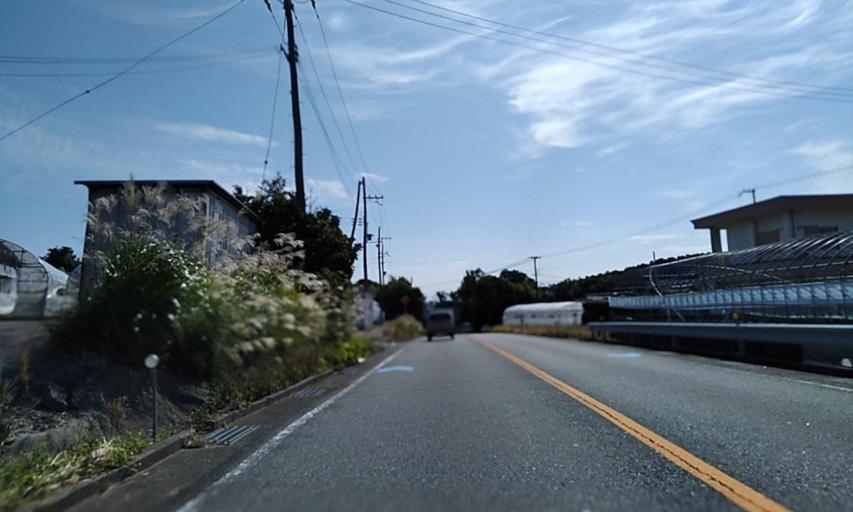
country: JP
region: Wakayama
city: Gobo
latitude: 33.8501
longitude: 135.1675
